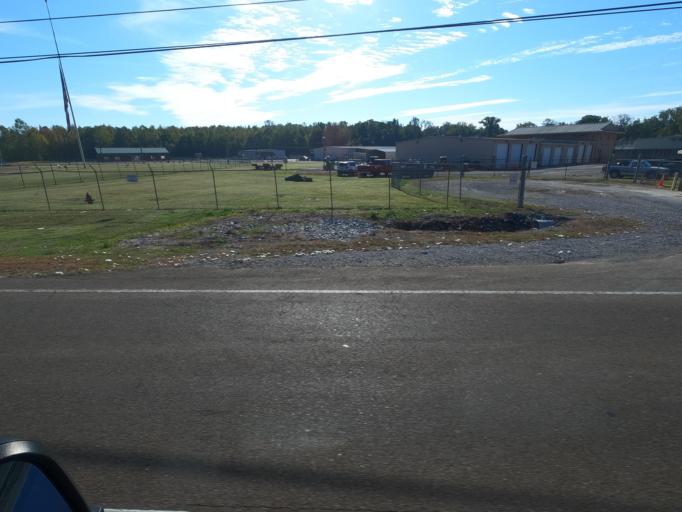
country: US
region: Tennessee
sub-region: Tipton County
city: Munford
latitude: 35.4131
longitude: -89.8294
